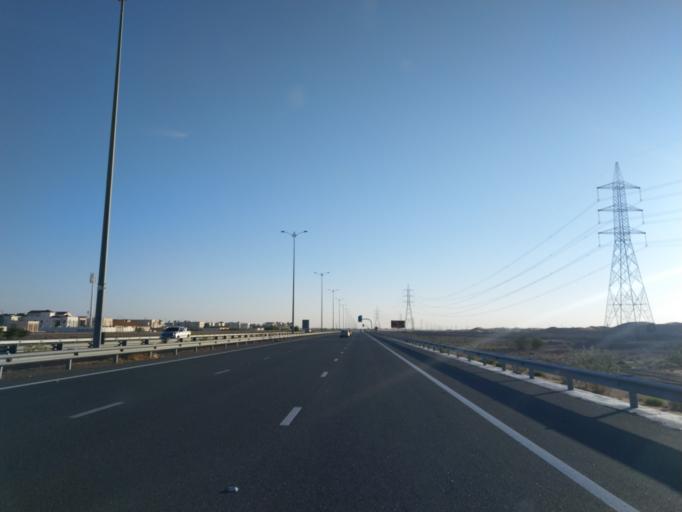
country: OM
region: Al Buraimi
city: Al Buraymi
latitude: 24.3601
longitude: 55.7872
